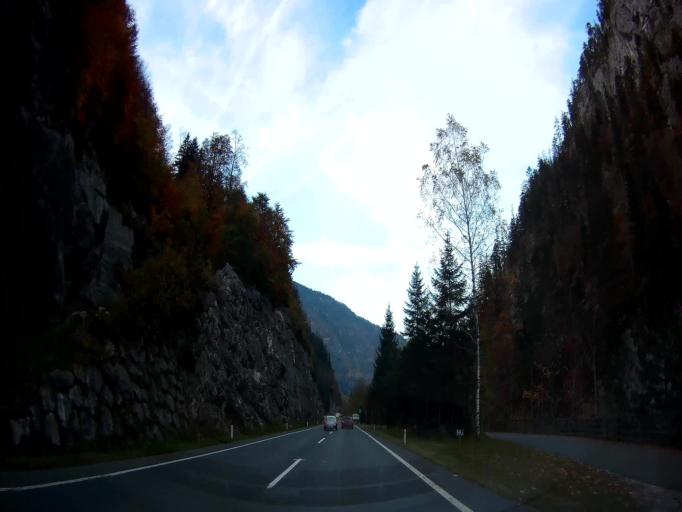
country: AT
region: Salzburg
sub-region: Politischer Bezirk Zell am See
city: Unken
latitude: 47.6334
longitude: 12.7277
